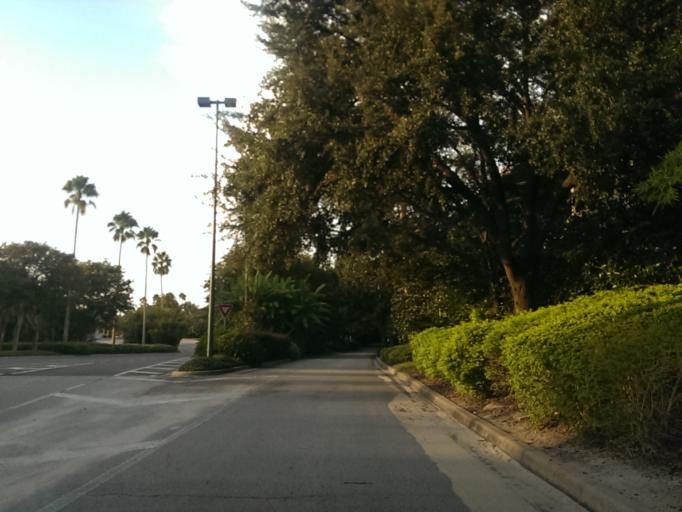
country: US
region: Florida
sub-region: Orange County
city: Tangelo Park
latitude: 28.4756
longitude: -81.4622
